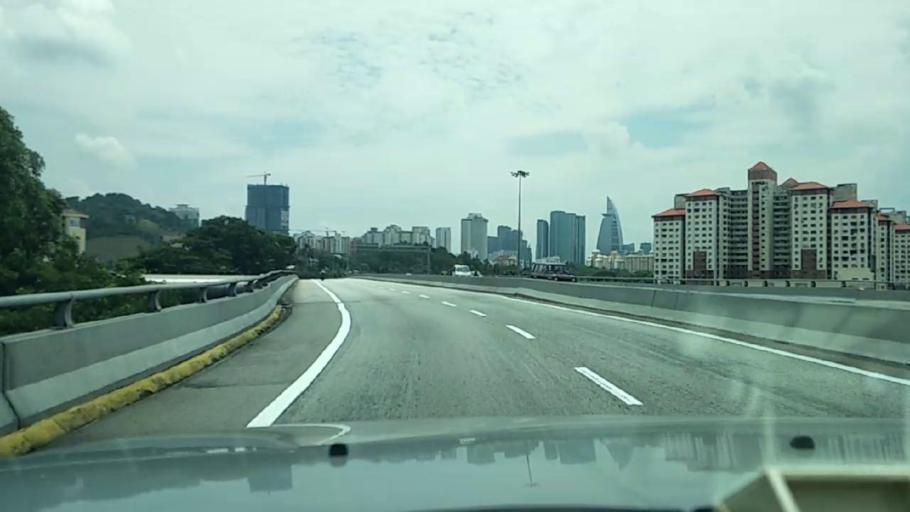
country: MY
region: Kuala Lumpur
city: Kuala Lumpur
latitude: 3.0926
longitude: 101.6712
